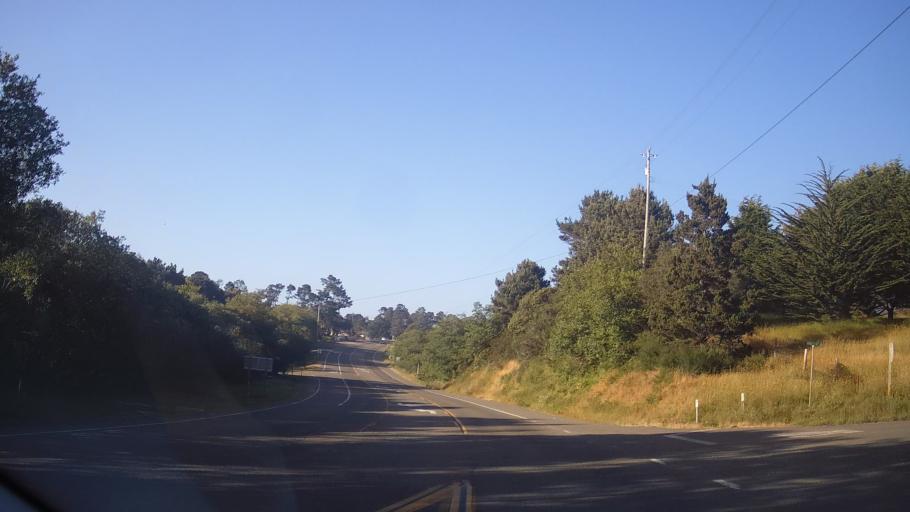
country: US
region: California
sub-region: Mendocino County
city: Fort Bragg
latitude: 39.4867
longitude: -123.7881
